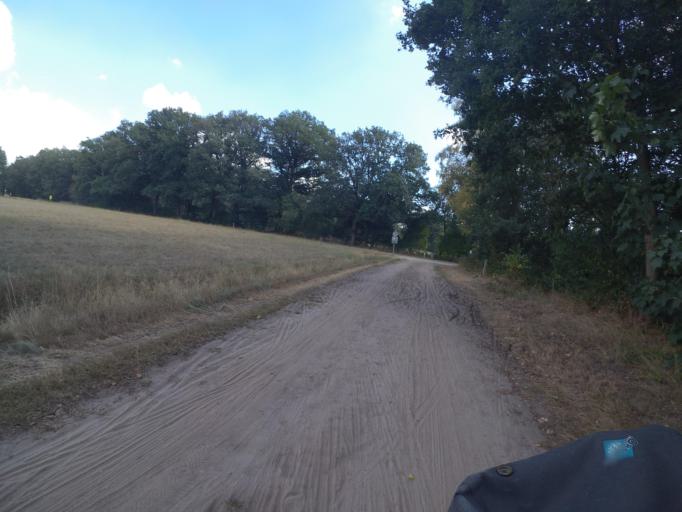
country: NL
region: Overijssel
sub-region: Gemeente Hof van Twente
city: Markelo
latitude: 52.2763
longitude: 6.4737
